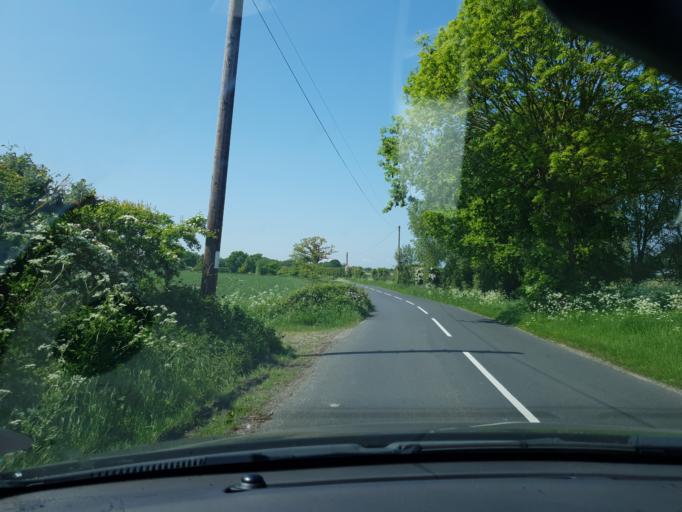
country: GB
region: England
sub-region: Essex
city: Great Bentley
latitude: 51.8552
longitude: 1.0789
